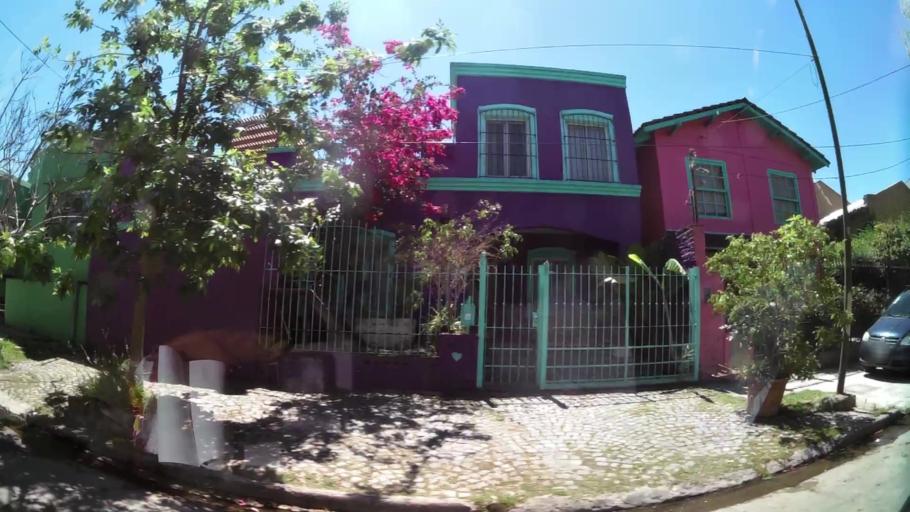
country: AR
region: Buenos Aires
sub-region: Partido de San Isidro
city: San Isidro
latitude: -34.4613
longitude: -58.5095
